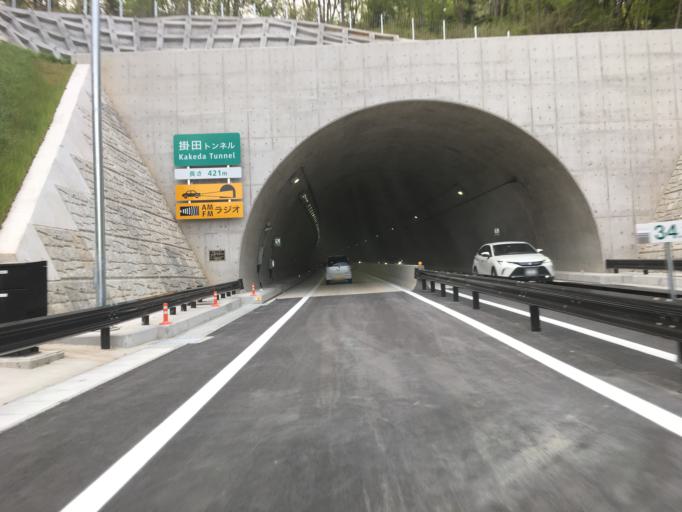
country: JP
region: Fukushima
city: Hobaramachi
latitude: 37.7778
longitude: 140.5801
